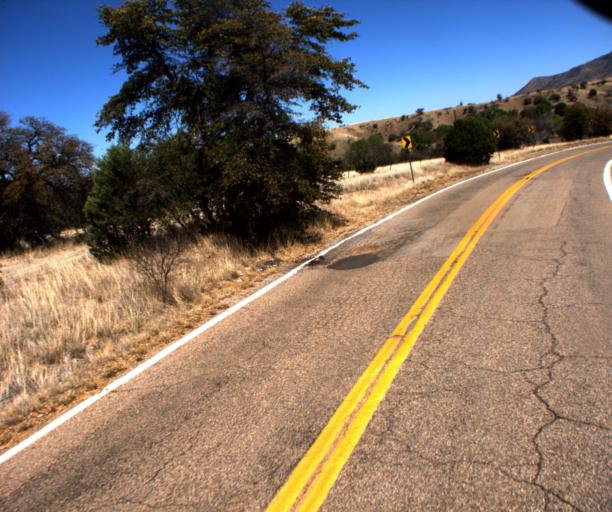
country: US
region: Arizona
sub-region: Cochise County
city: Huachuca City
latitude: 31.5553
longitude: -110.5301
